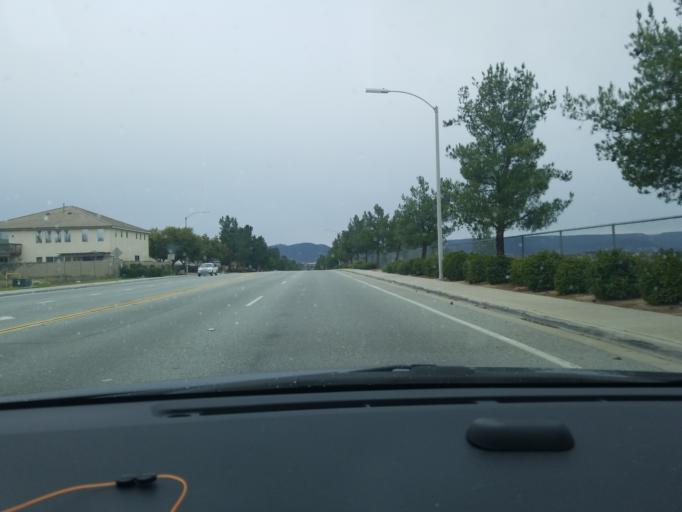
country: US
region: California
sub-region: Riverside County
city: Murrieta Hot Springs
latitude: 33.5507
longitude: -117.1477
